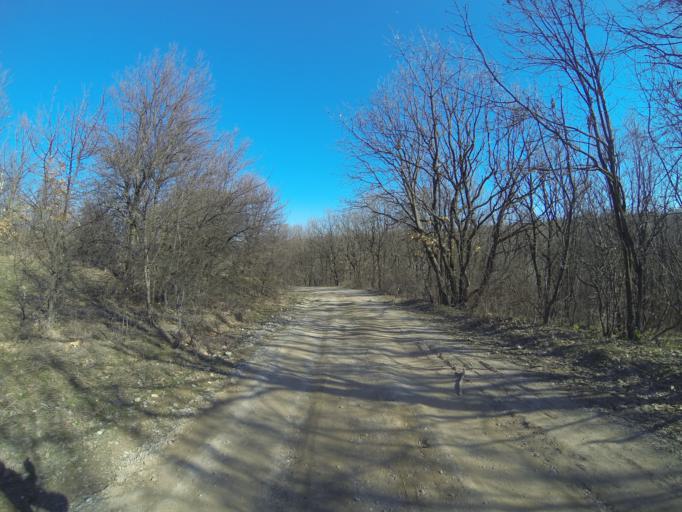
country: RO
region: Dolj
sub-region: Comuna Tuglui
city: Tuglui
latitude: 44.1441
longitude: 23.8289
